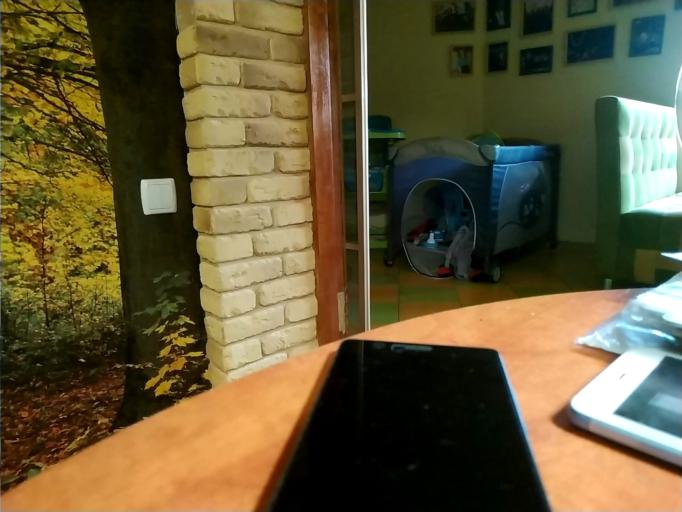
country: RU
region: Kaluga
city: Khvastovichi
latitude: 53.6661
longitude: 35.4443
